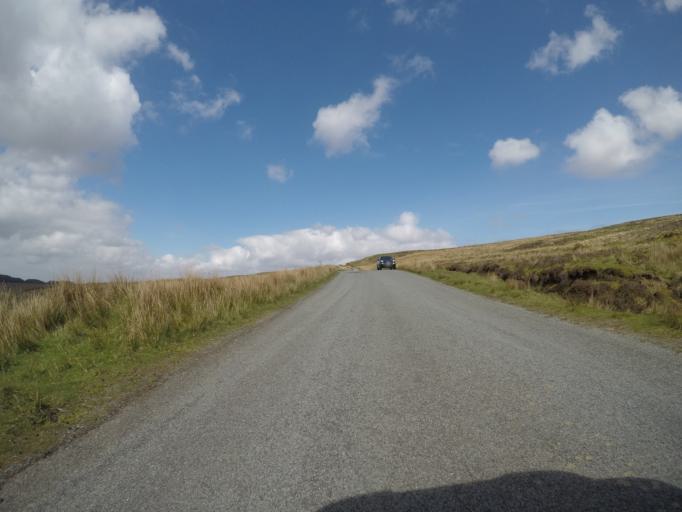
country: GB
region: Scotland
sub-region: Highland
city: Isle of Skye
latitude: 57.4164
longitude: -6.2951
